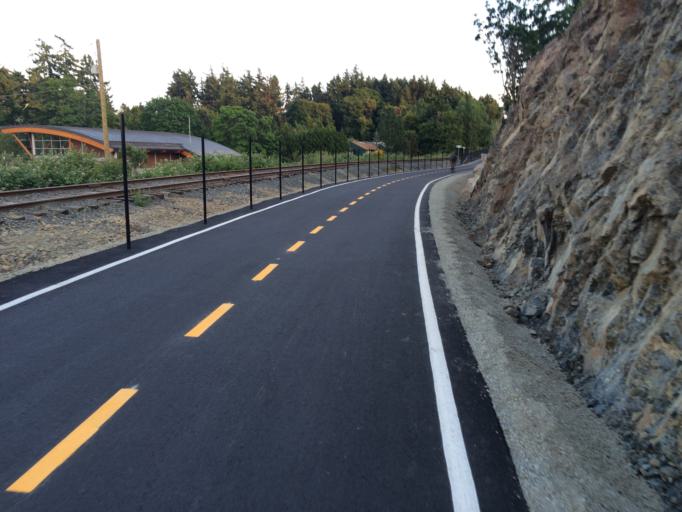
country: CA
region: British Columbia
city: Colwood
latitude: 48.4540
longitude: -123.4305
